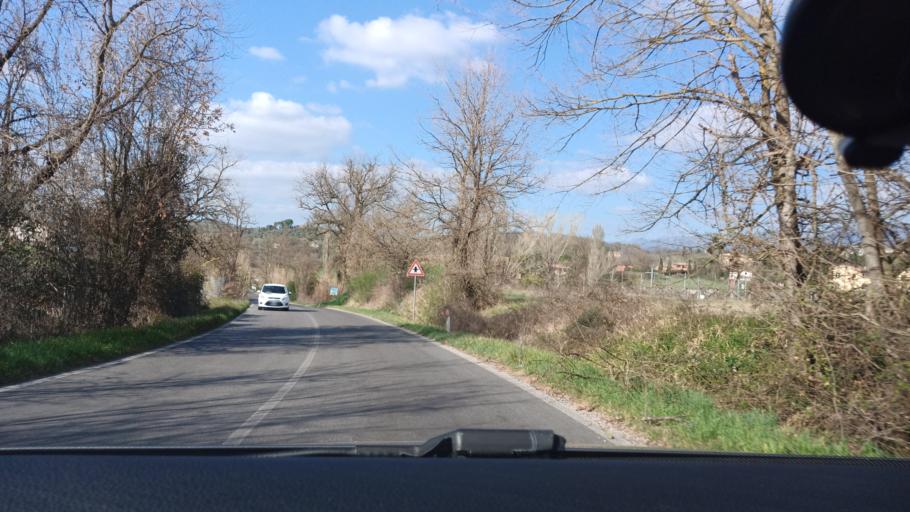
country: IT
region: Latium
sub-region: Citta metropolitana di Roma Capitale
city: Torrita Tiberina
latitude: 42.2572
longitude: 12.6394
